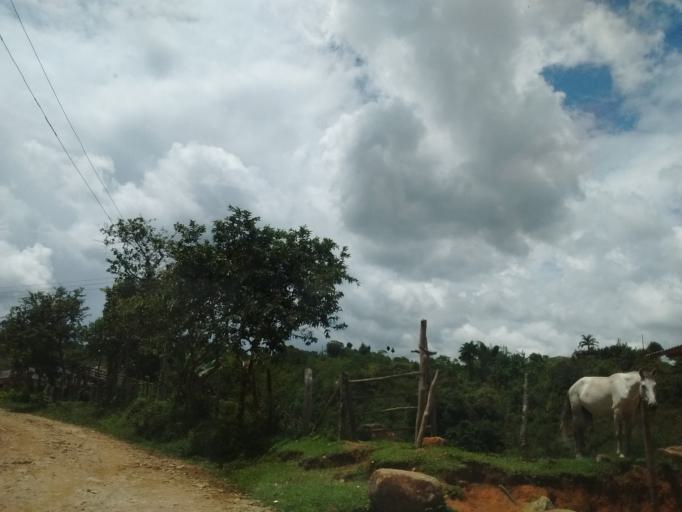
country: CO
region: Cauca
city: Villa Rica
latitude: 2.6020
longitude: -76.7564
